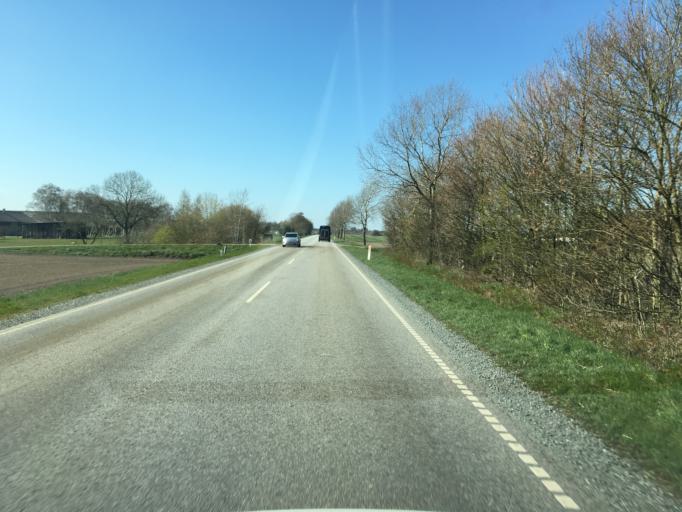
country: DK
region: South Denmark
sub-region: Aabenraa Kommune
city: Tinglev
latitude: 54.9566
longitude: 9.3352
